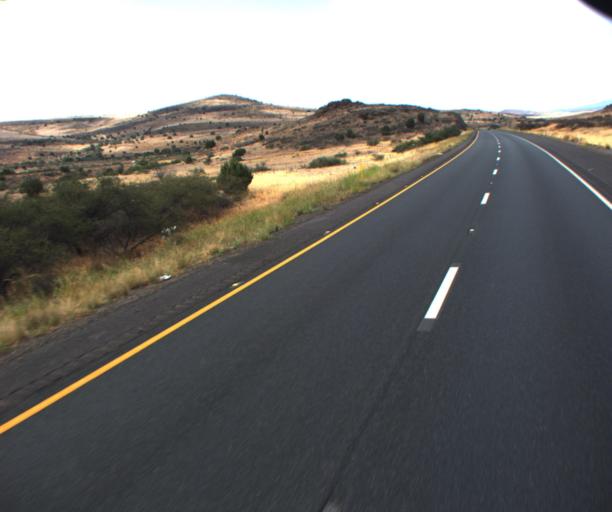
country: US
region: Arizona
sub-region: Yavapai County
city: Cordes Lakes
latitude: 34.4761
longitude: -112.0239
